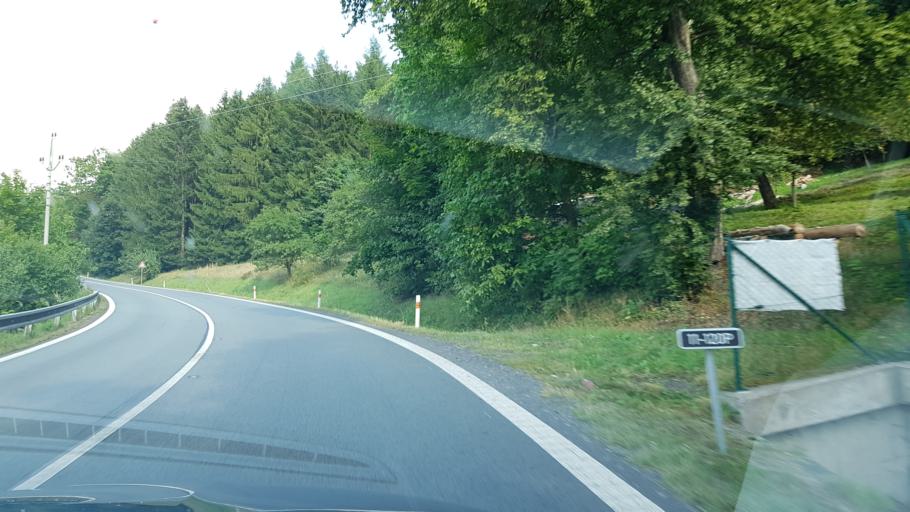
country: CZ
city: Vamberk
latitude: 50.1208
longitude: 16.3124
